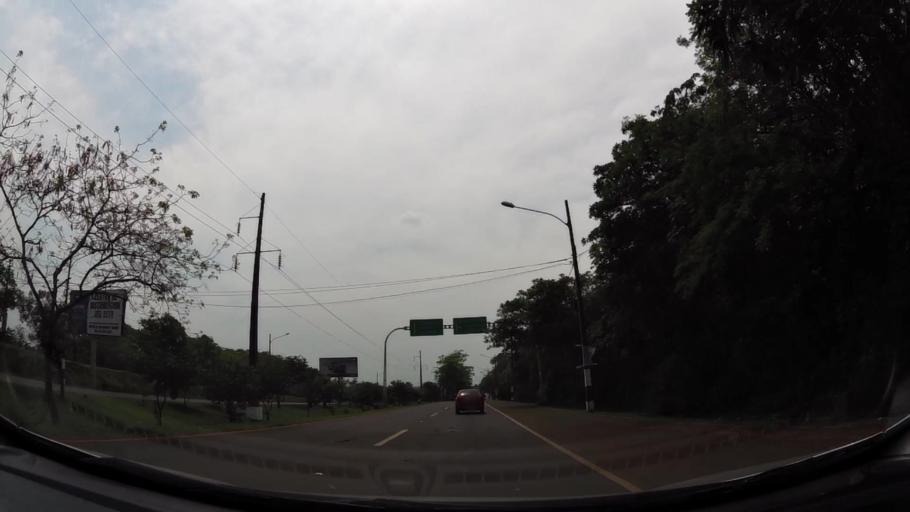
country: PY
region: Alto Parana
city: Ciudad del Este
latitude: -25.4804
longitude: -54.6260
